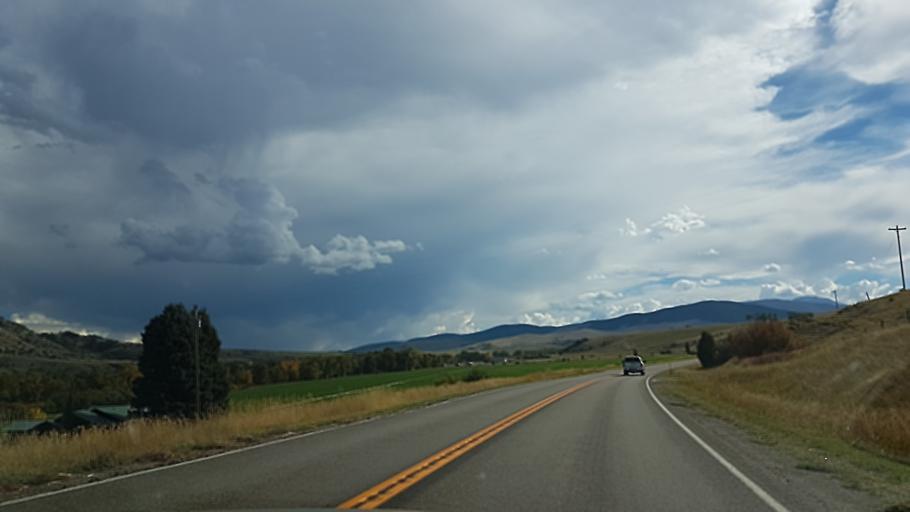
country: US
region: Montana
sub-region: Jefferson County
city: Whitehall
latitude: 45.8211
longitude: -111.9330
